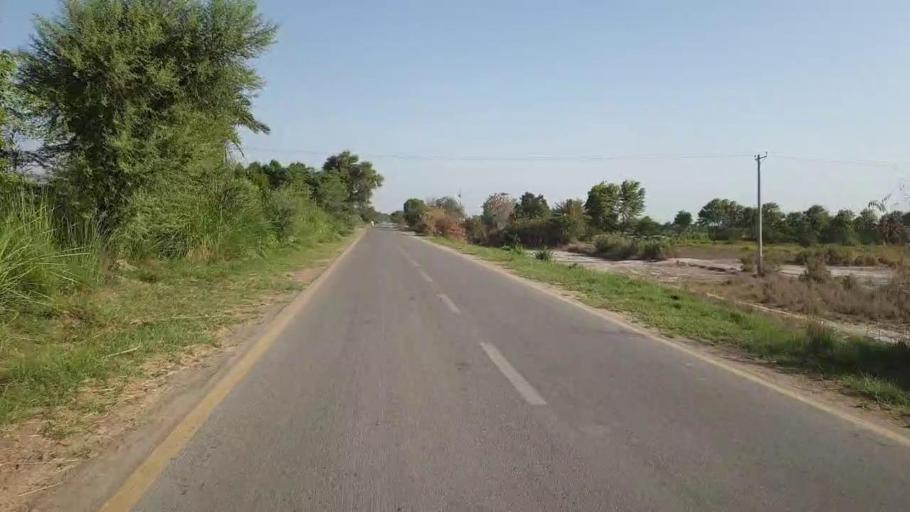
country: PK
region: Sindh
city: Daur
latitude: 26.4558
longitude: 68.4507
